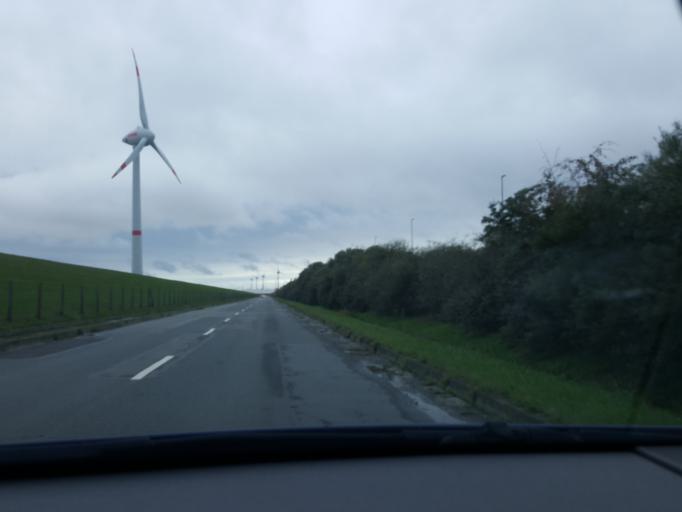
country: DE
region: Lower Saxony
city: Emden
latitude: 53.3333
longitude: 7.2182
